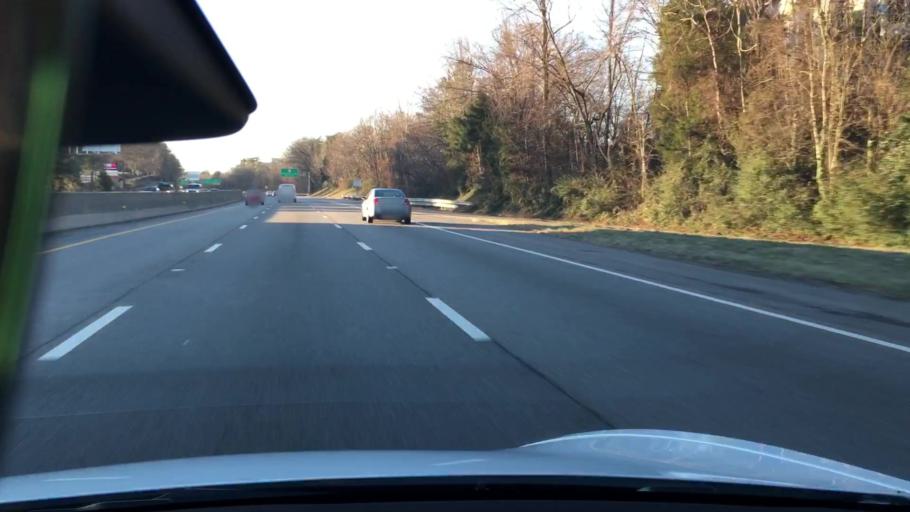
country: US
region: Virginia
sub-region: Chesterfield County
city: Bon Air
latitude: 37.5134
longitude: -77.5286
